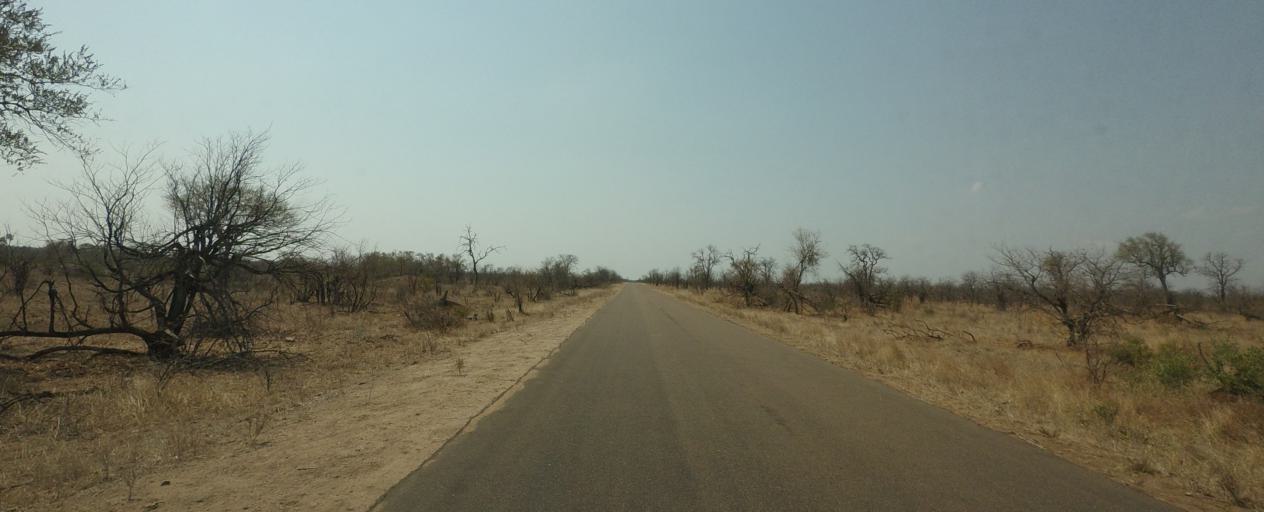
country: ZA
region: Limpopo
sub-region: Mopani District Municipality
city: Phalaborwa
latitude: -23.3660
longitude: 31.3198
